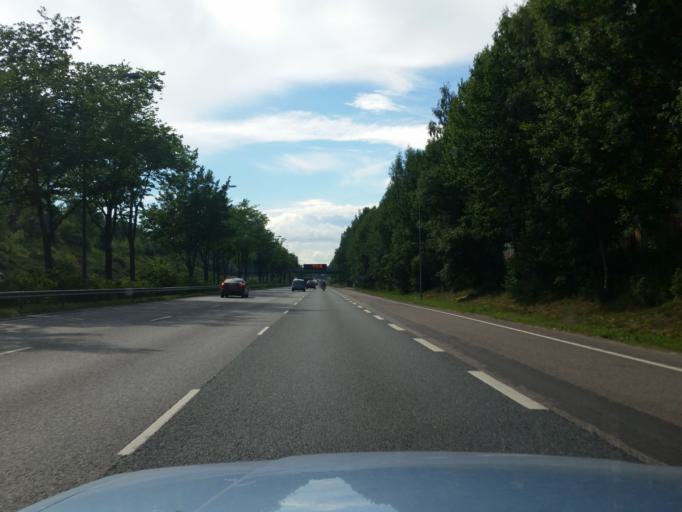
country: FI
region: Uusimaa
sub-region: Helsinki
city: Teekkarikylae
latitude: 60.2347
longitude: 24.8827
